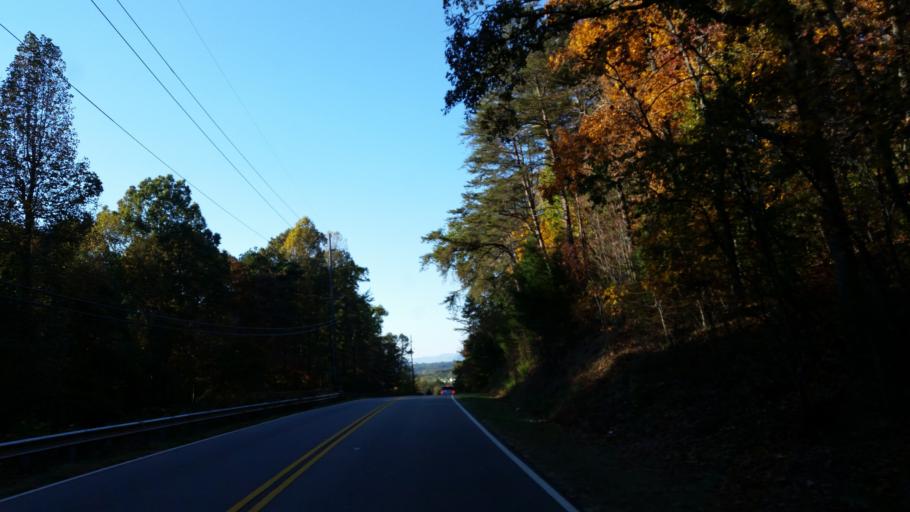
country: US
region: Georgia
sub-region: Gilmer County
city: Ellijay
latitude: 34.6717
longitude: -84.4751
